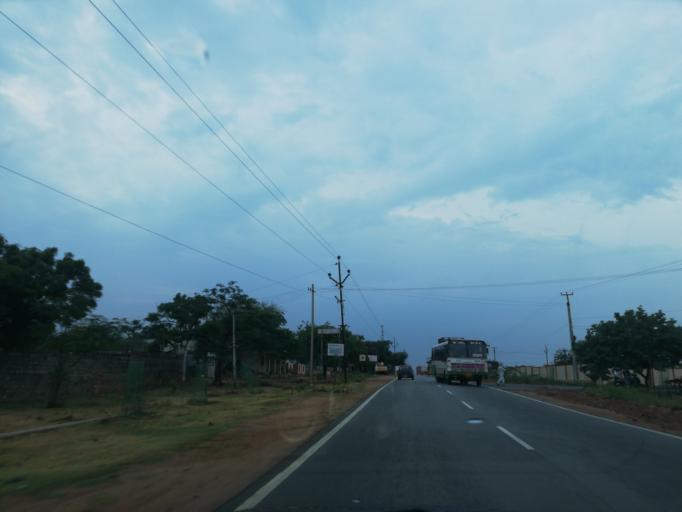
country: IN
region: Andhra Pradesh
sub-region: Guntur
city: Macherla
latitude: 16.6163
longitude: 79.2961
